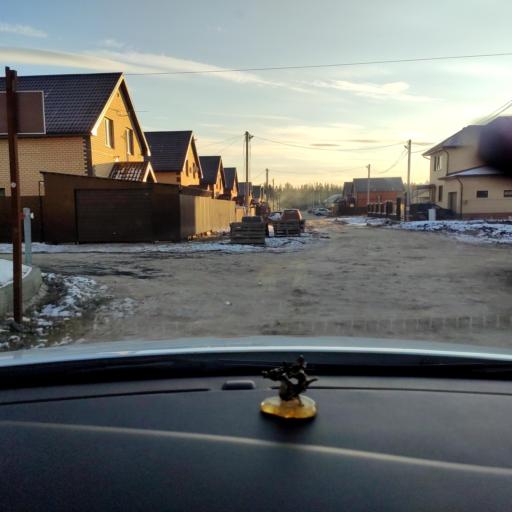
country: RU
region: Tatarstan
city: Stolbishchi
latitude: 55.6056
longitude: 49.1410
